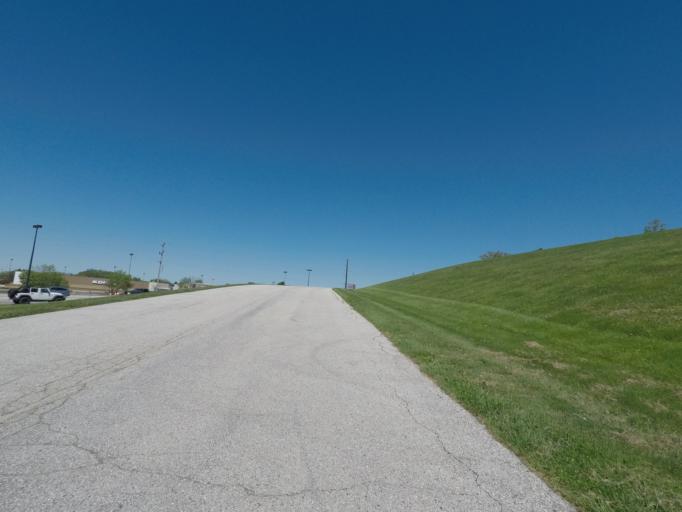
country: US
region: Wisconsin
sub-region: Sheboygan County
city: Sheboygan
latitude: 43.7526
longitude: -87.7493
